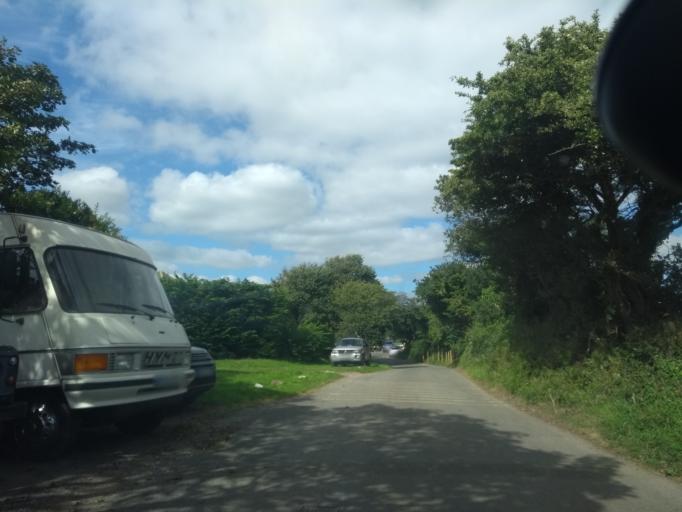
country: GB
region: England
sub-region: Devon
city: Modbury
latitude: 50.2957
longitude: -3.8954
